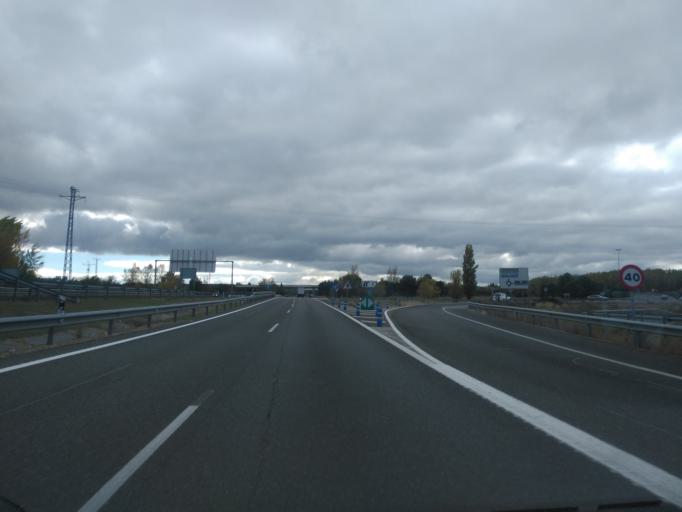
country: ES
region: Castille and Leon
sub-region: Provincia de Palencia
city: Villamuriel de Cerrato
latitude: 41.9418
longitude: -4.5037
